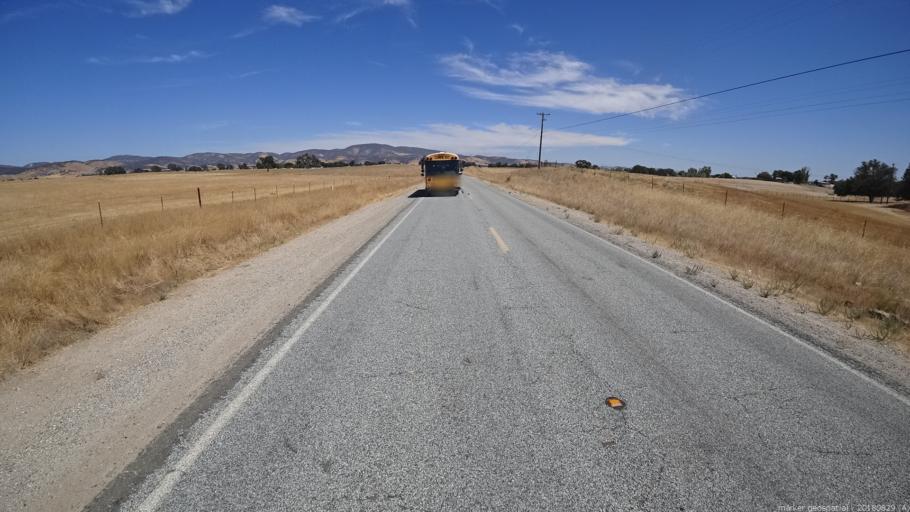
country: US
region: California
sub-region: Monterey County
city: King City
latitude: 35.9370
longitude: -121.0962
